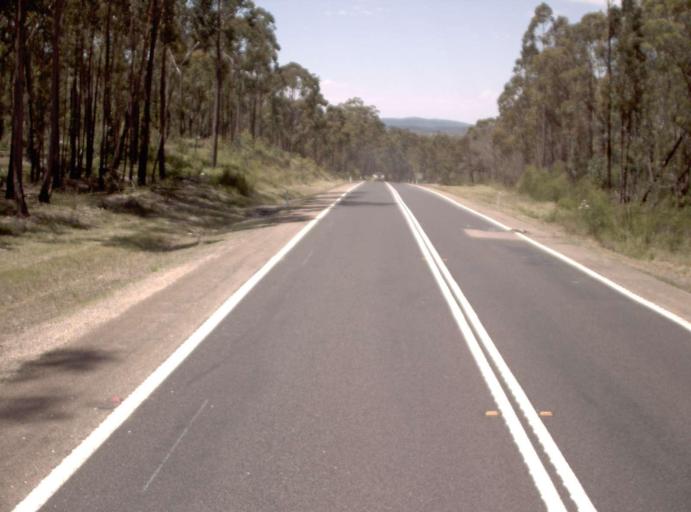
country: AU
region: New South Wales
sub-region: Bombala
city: Bombala
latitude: -37.5660
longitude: 149.1150
